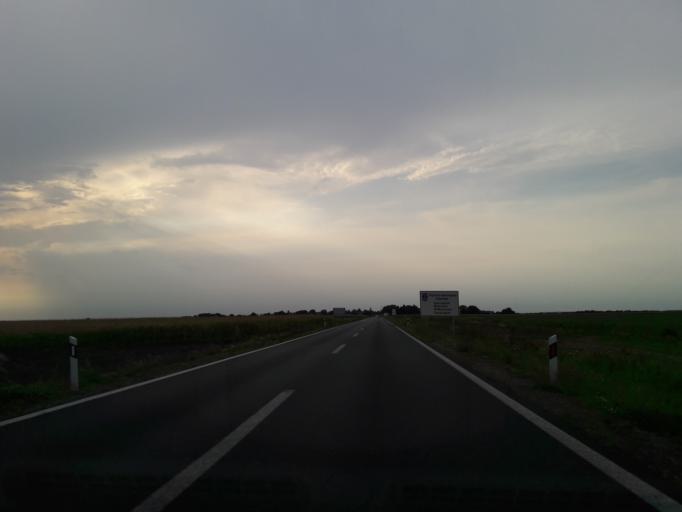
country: HR
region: Vukovarsko-Srijemska
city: Bobota
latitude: 45.4671
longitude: 18.8440
